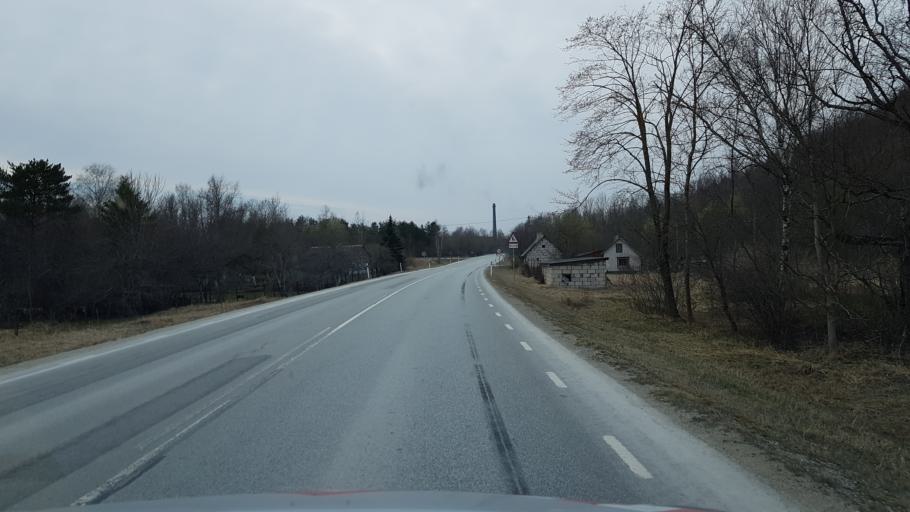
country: EE
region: Ida-Virumaa
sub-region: Kivioli linn
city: Kivioli
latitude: 59.3610
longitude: 26.9587
